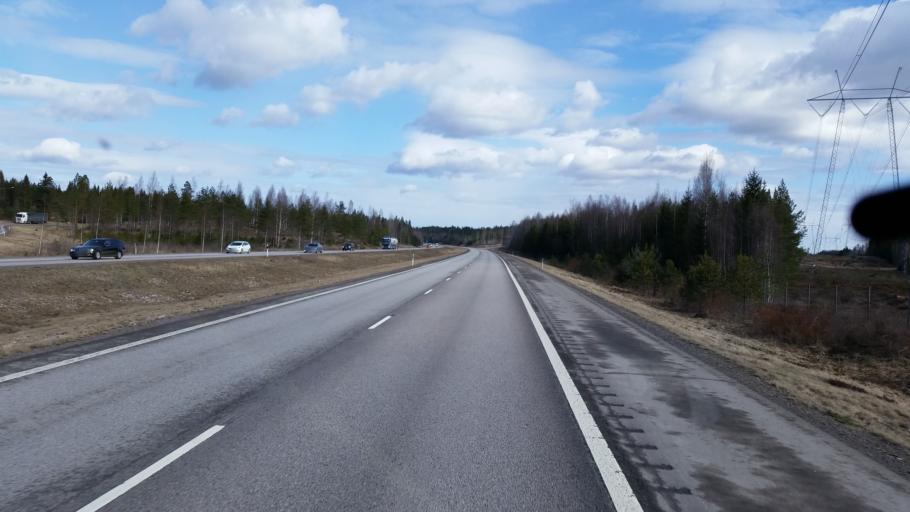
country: FI
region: Uusimaa
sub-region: Porvoo
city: Porvoo
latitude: 60.4422
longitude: 25.8274
